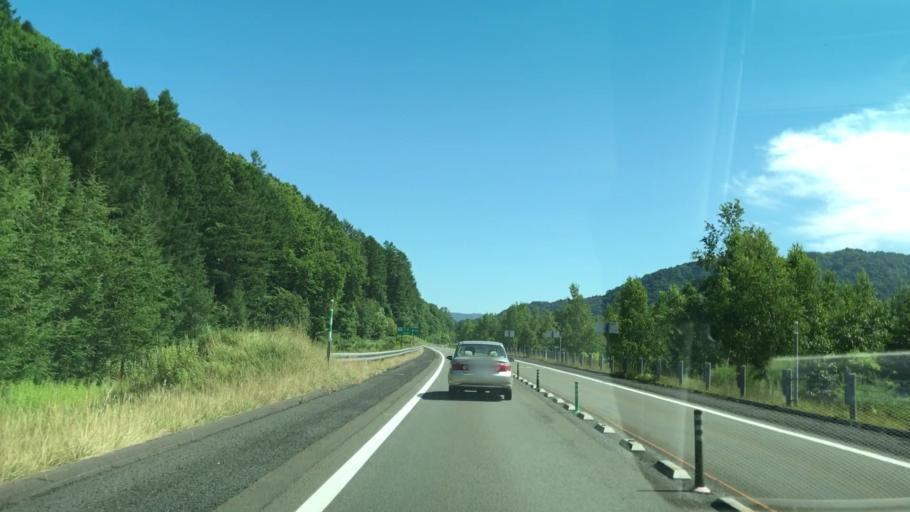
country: JP
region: Hokkaido
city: Chitose
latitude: 42.9101
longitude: 142.0152
